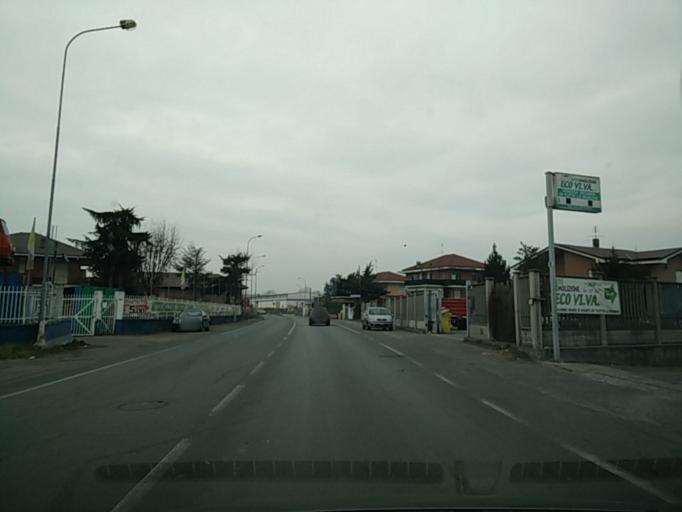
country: IT
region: Piedmont
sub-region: Provincia di Torino
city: Settimo Torinese
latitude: 45.1522
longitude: 7.7310
